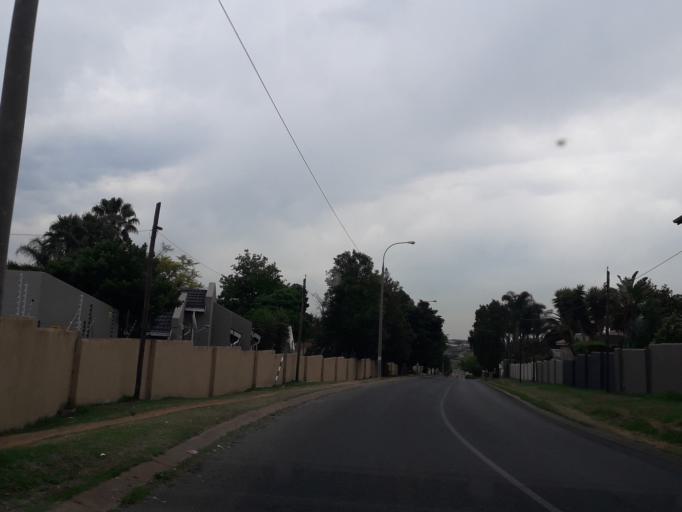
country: ZA
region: Gauteng
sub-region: City of Johannesburg Metropolitan Municipality
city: Roodepoort
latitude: -26.1018
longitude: 27.9242
